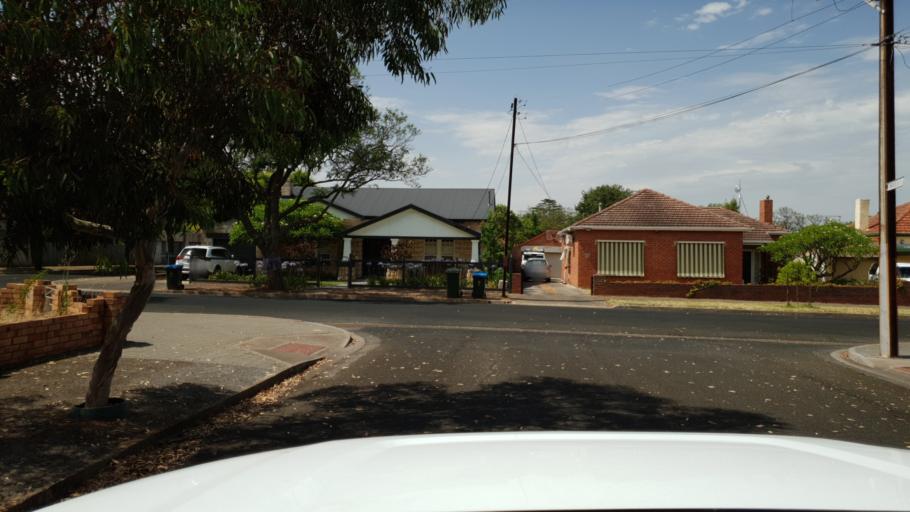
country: AU
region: South Australia
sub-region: Mitcham
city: Clarence Gardens
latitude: -34.9742
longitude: 138.5848
